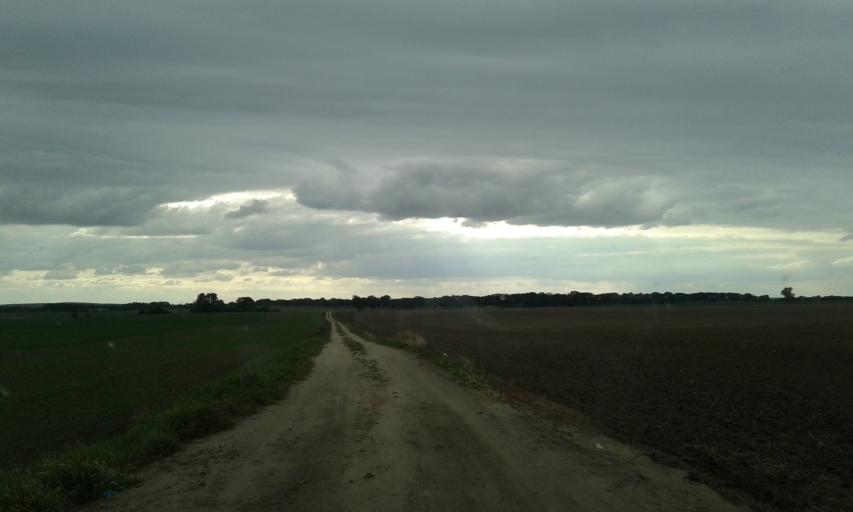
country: PL
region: West Pomeranian Voivodeship
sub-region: Powiat pyrzycki
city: Przelewice
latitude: 53.1881
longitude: 15.0617
